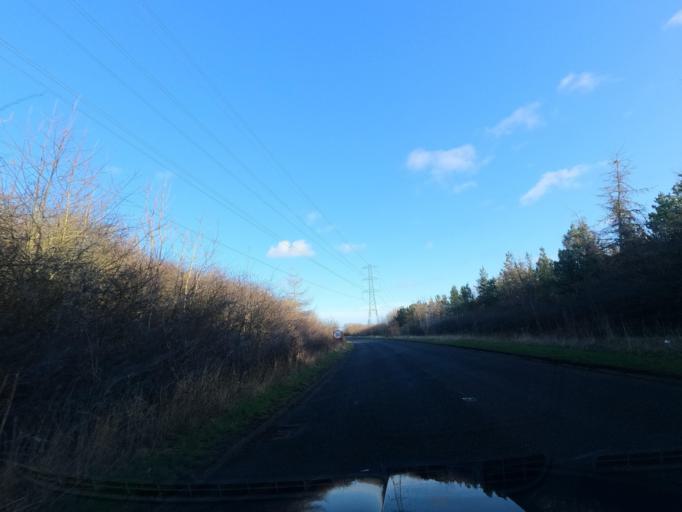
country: GB
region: England
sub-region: Northumberland
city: Blyth
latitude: 55.1454
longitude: -1.5450
